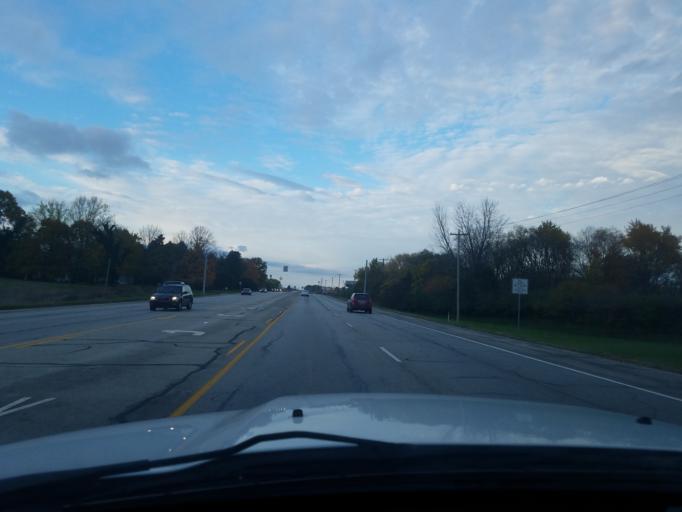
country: US
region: Indiana
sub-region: Shelby County
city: Shelbyville
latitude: 39.5404
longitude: -85.7753
